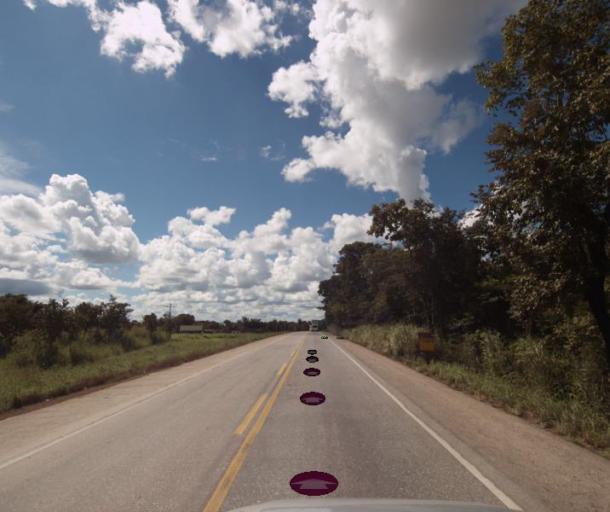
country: BR
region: Goias
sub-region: Porangatu
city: Porangatu
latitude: -13.6004
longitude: -49.0419
